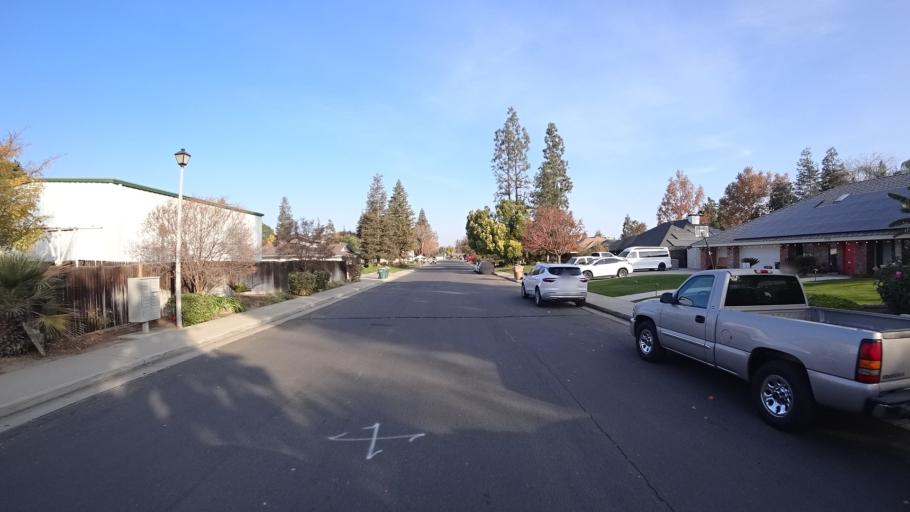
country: US
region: California
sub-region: Kern County
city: Rosedale
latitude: 35.3739
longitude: -119.1324
